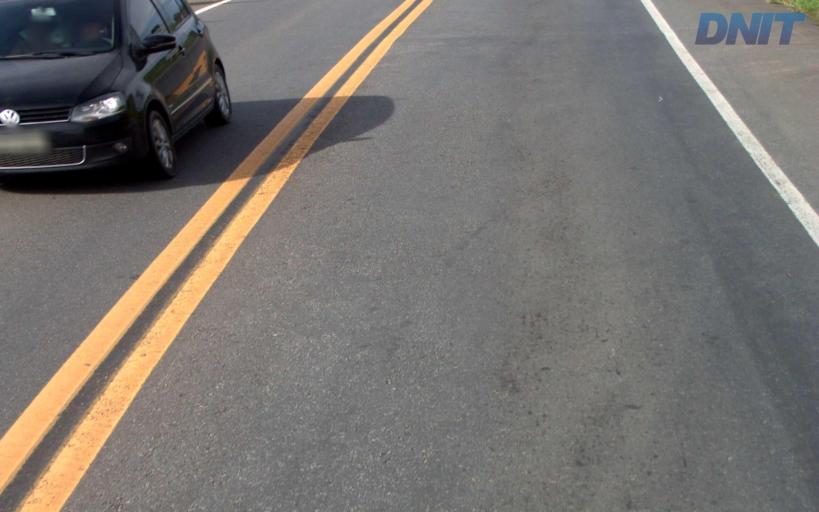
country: BR
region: Minas Gerais
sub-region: Belo Oriente
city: Belo Oriente
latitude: -19.2105
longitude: -42.3052
